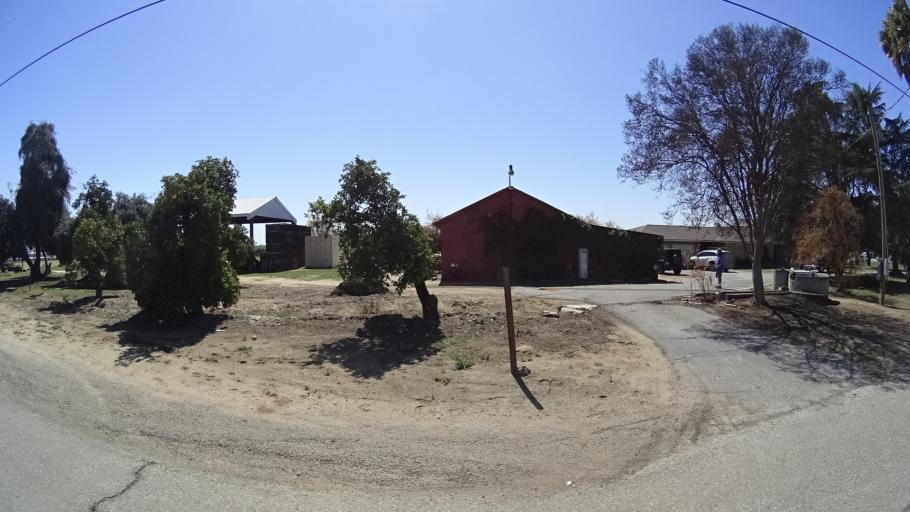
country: US
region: California
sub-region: Fresno County
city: West Park
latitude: 36.7065
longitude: -119.8544
